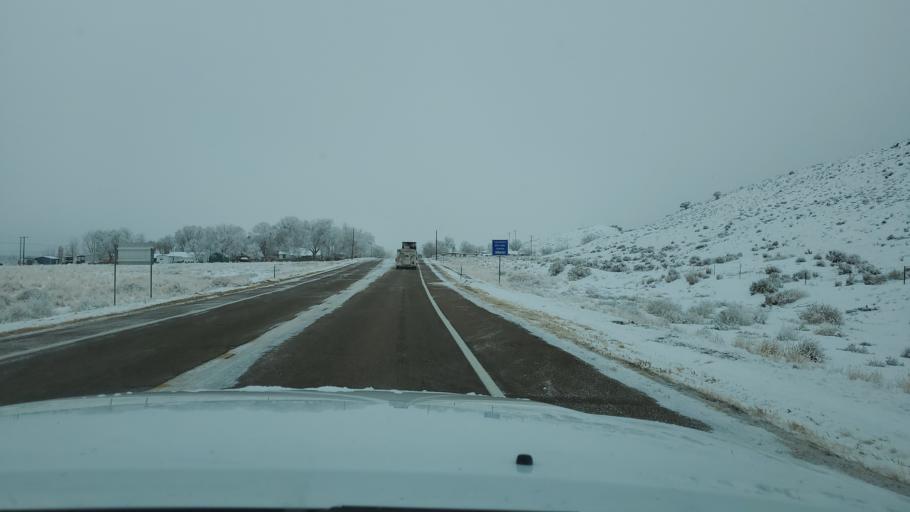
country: US
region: Colorado
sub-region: Rio Blanco County
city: Rangely
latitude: 40.2445
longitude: -109.0000
